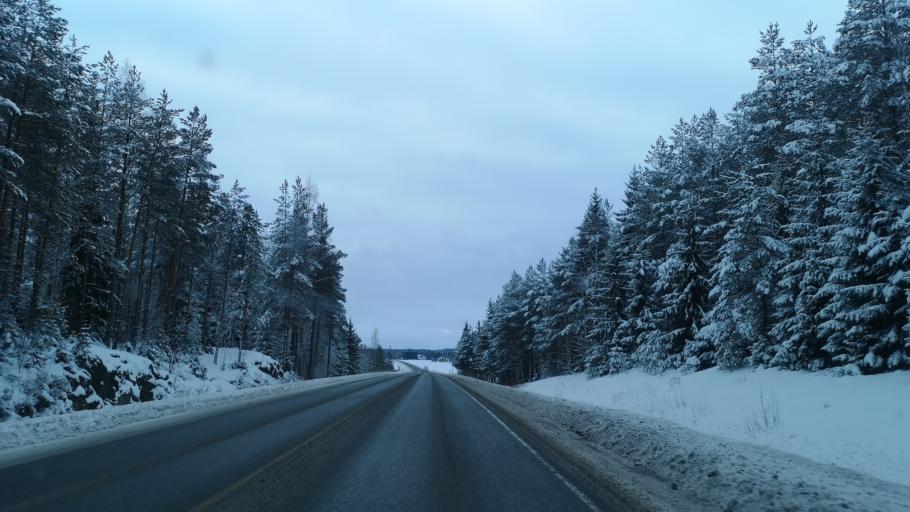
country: FI
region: Varsinais-Suomi
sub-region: Loimaa
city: Loimaa
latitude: 60.8699
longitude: 23.0595
